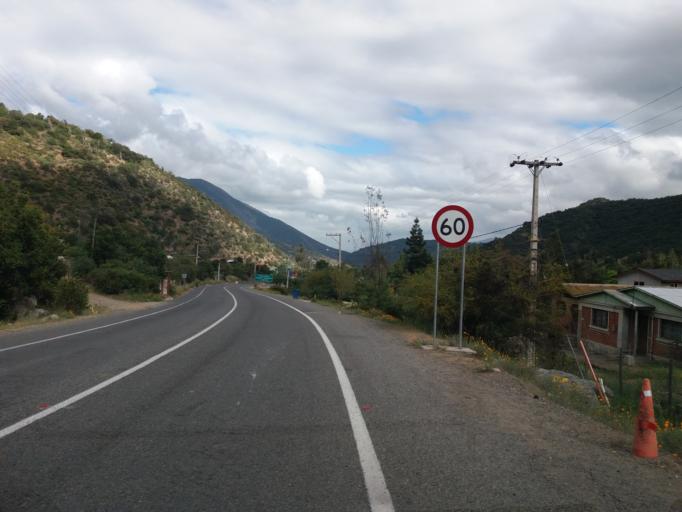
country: CL
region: Valparaiso
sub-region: Provincia de Marga Marga
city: Limache
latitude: -33.0613
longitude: -71.0764
